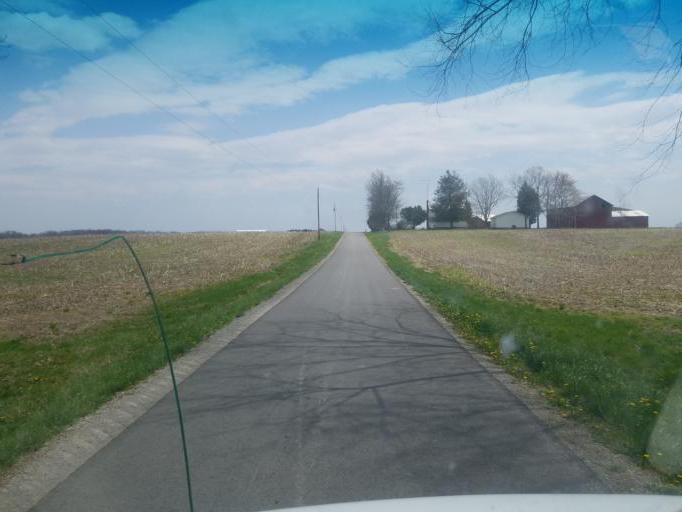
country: US
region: Ohio
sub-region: Hardin County
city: Forest
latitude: 40.7737
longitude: -83.4096
